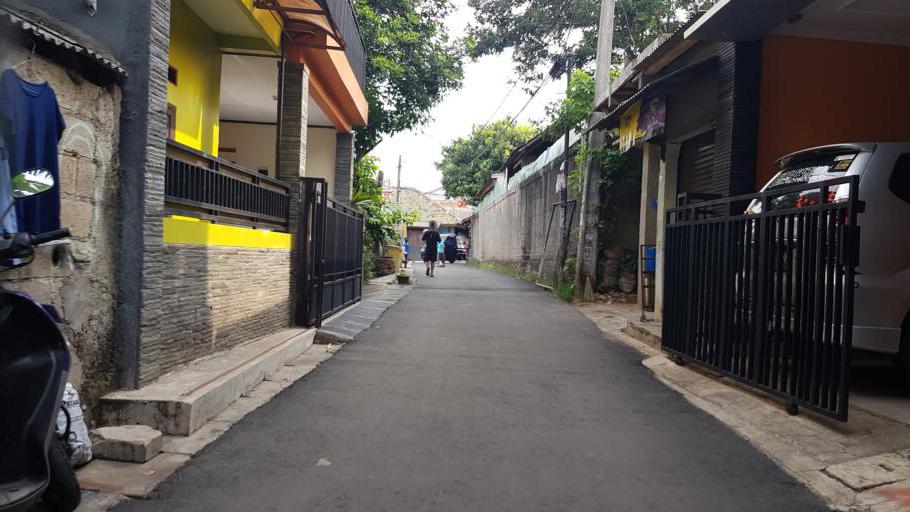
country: ID
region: West Java
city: Pamulang
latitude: -6.3233
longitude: 106.7998
